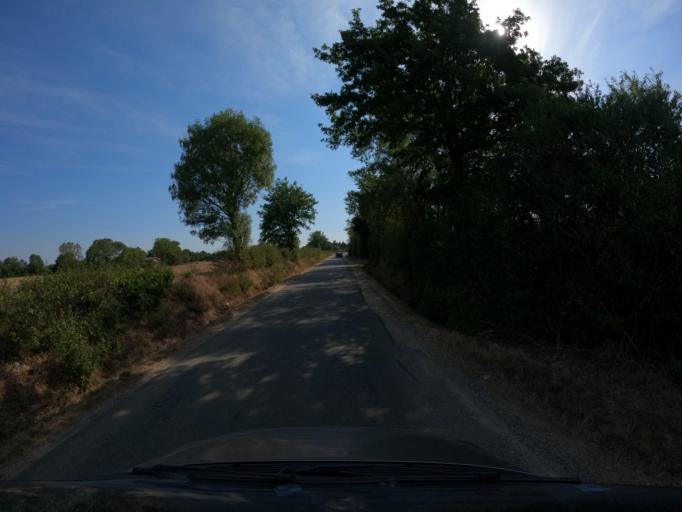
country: FR
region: Pays de la Loire
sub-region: Departement de la Vendee
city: Commequiers
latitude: 46.8121
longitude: -1.8320
